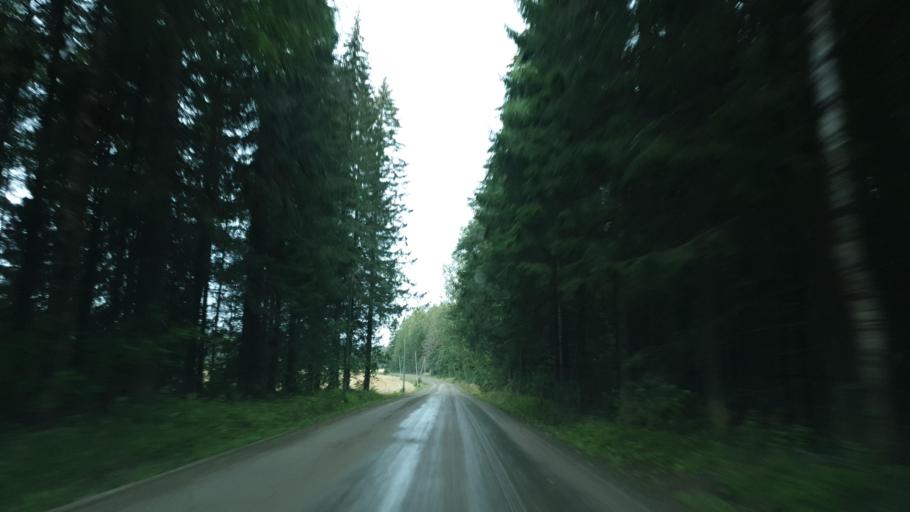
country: FI
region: Northern Savo
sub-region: Kuopio
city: Nilsiae
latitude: 63.1534
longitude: 28.1962
